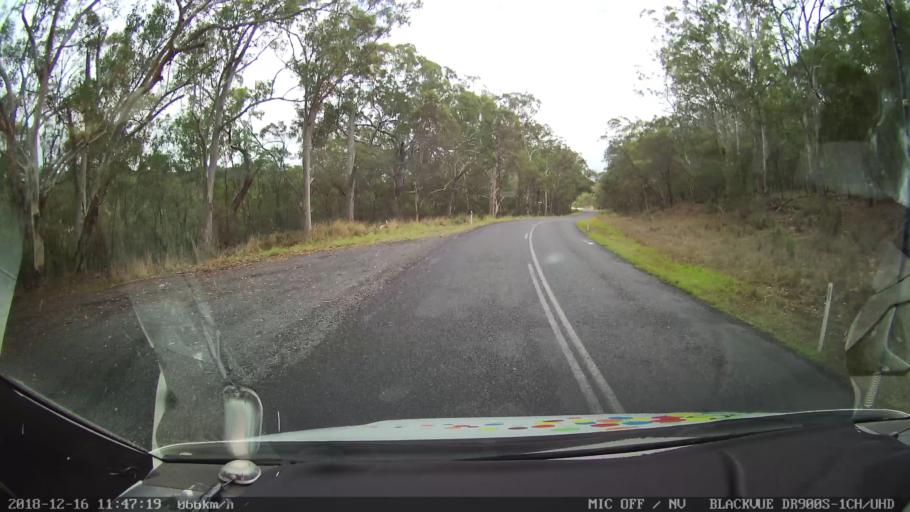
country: AU
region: New South Wales
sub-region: Tenterfield Municipality
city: Carrolls Creek
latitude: -28.9219
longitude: 152.2368
